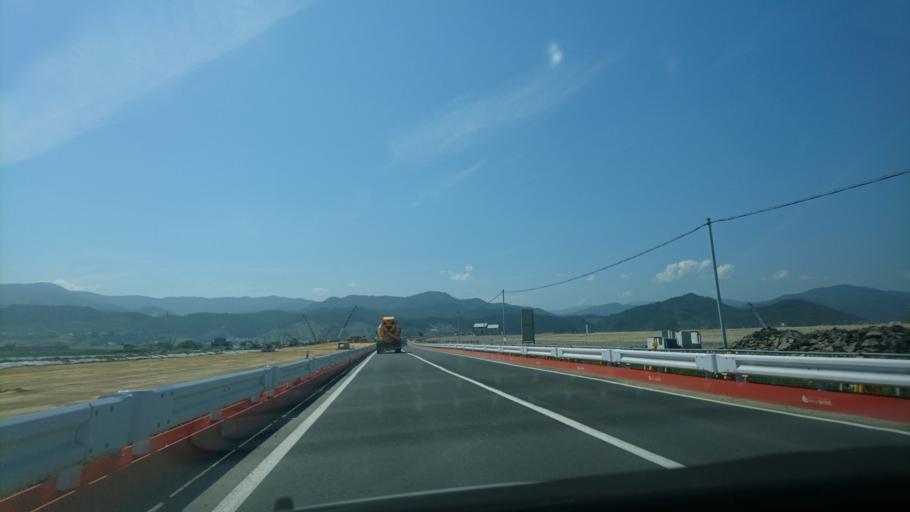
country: JP
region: Iwate
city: Ofunato
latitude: 39.0096
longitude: 141.6357
